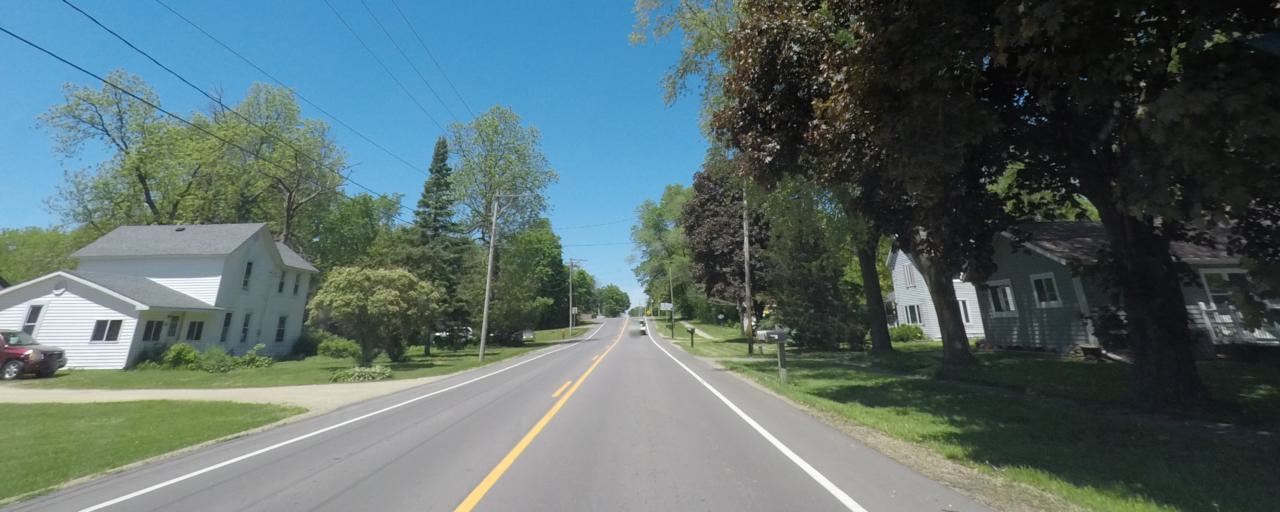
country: US
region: Wisconsin
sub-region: Green County
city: Brooklyn
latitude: 42.8489
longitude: -89.3692
